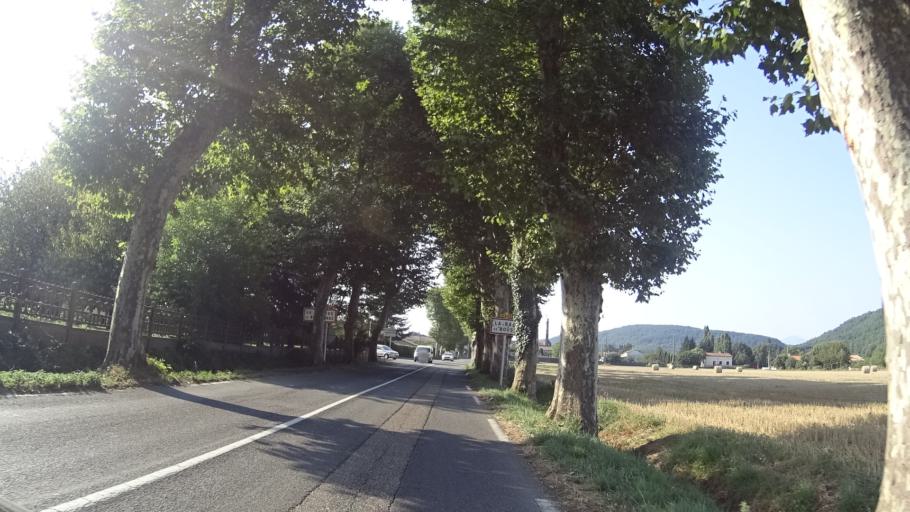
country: FR
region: Midi-Pyrenees
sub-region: Departement de l'Ariege
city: Mirepoix
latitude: 43.0569
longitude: 1.8846
